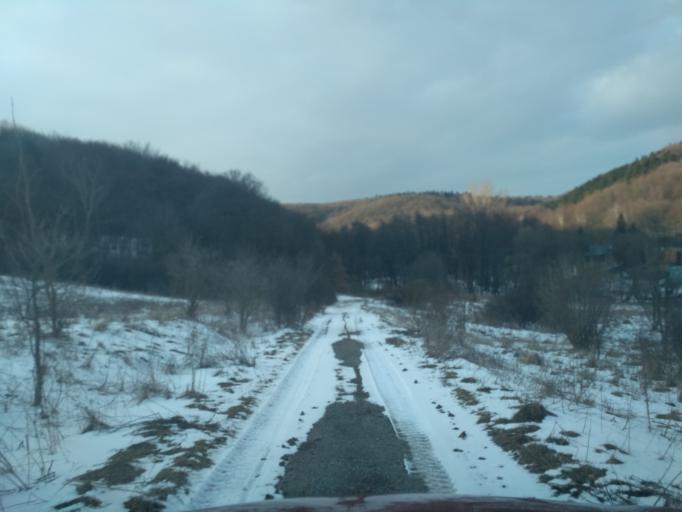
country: SK
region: Kosicky
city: Kosice
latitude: 48.7446
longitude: 21.1505
